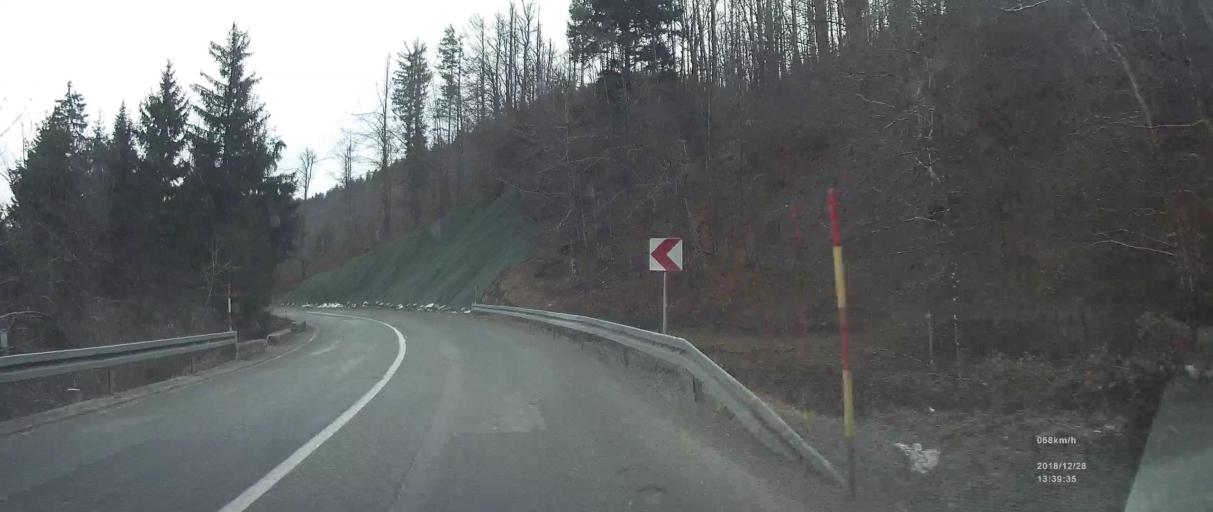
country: HR
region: Primorsko-Goranska
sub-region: Grad Delnice
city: Delnice
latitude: 45.3514
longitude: 14.7385
